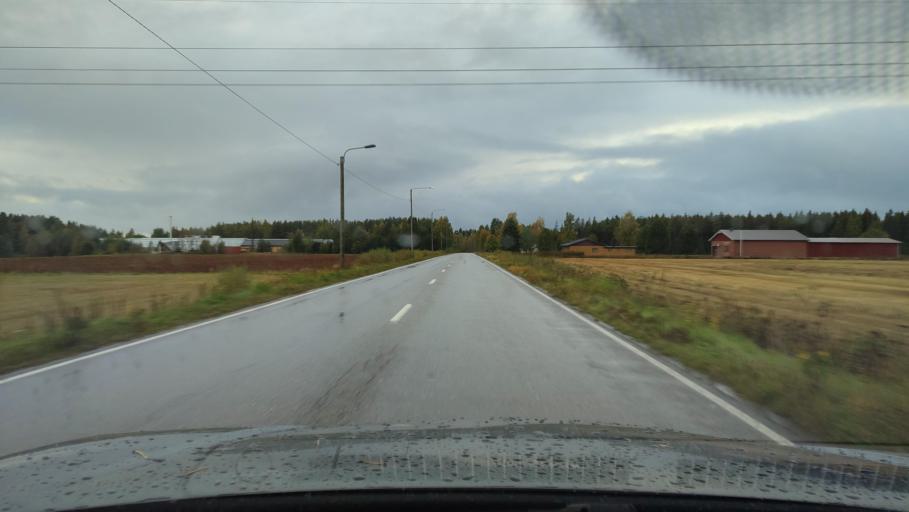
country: FI
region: Southern Ostrobothnia
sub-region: Suupohja
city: Karijoki
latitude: 62.2378
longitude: 21.6086
